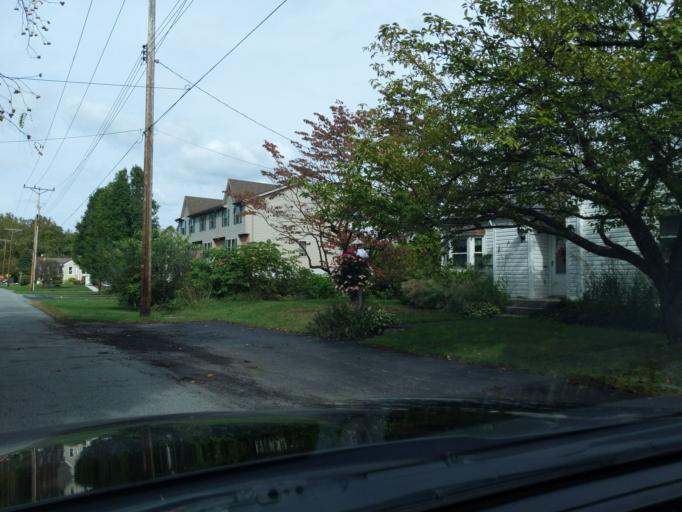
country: US
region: Pennsylvania
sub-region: Blair County
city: Hollidaysburg
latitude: 40.4291
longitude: -78.4044
